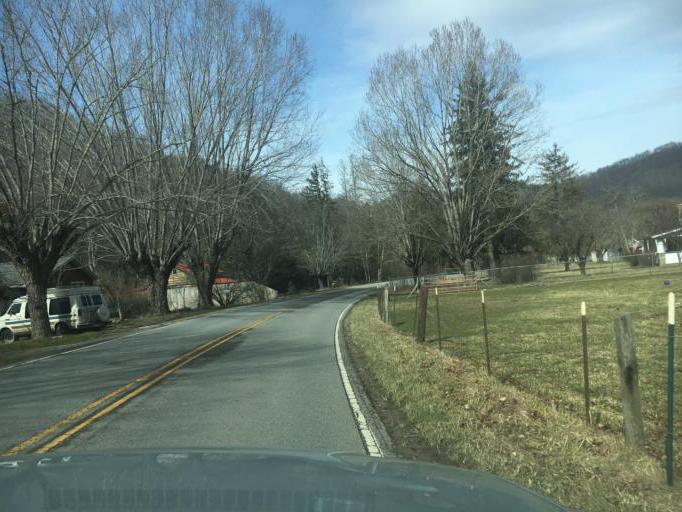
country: US
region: North Carolina
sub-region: Haywood County
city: Canton
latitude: 35.4528
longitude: -82.8406
